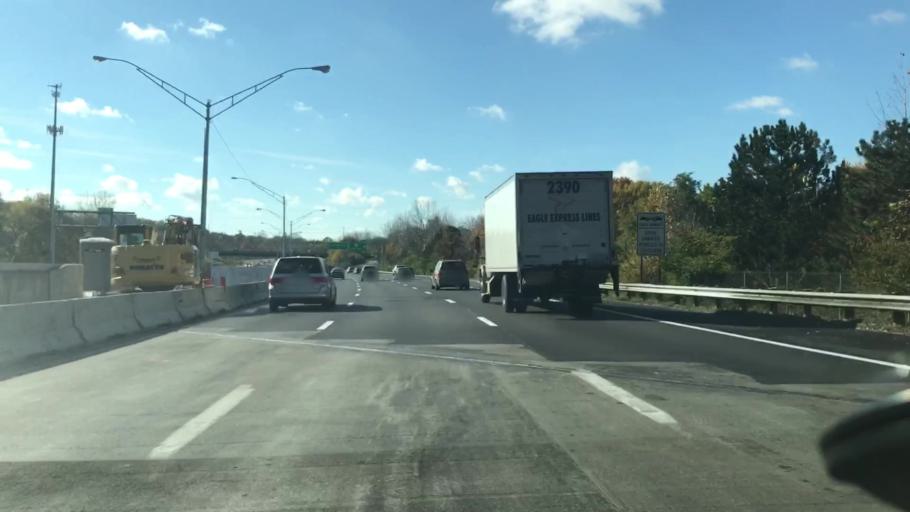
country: US
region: Ohio
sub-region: Franklin County
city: Bexley
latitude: 39.9897
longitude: -82.9379
